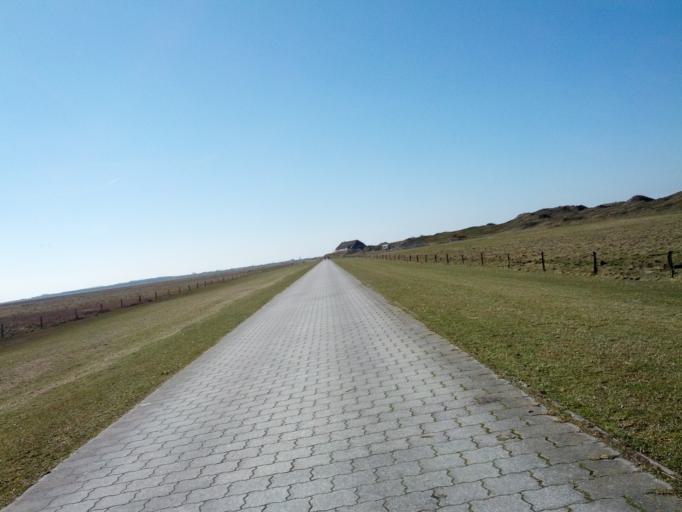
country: DE
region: Lower Saxony
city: Langeoog
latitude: 53.7499
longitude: 7.5470
